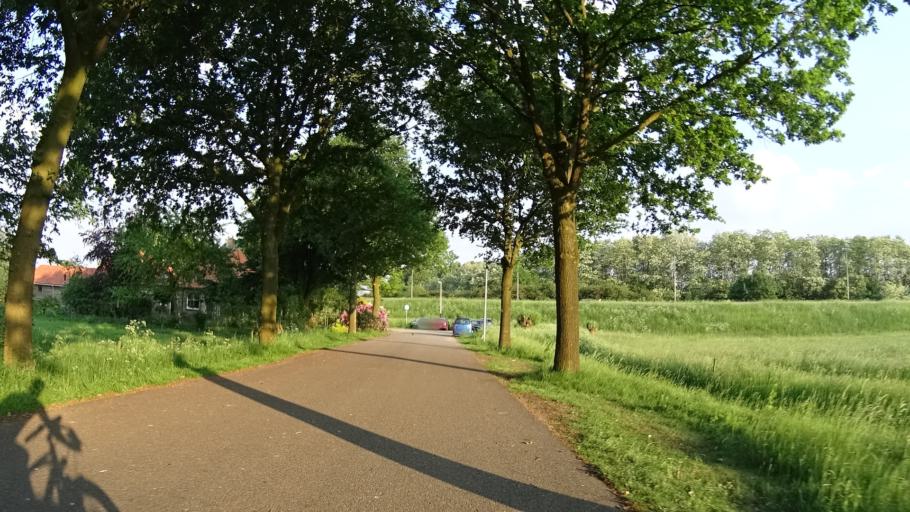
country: NL
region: Gelderland
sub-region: Gemeente Maasdriel
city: Hedel
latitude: 51.6989
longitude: 5.2434
